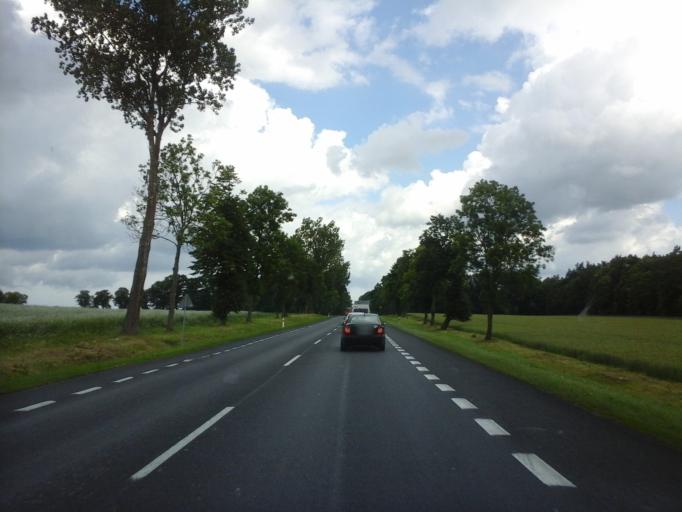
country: PL
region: West Pomeranian Voivodeship
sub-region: Powiat bialogardzki
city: Bialogard
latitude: 54.0955
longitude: 15.9928
